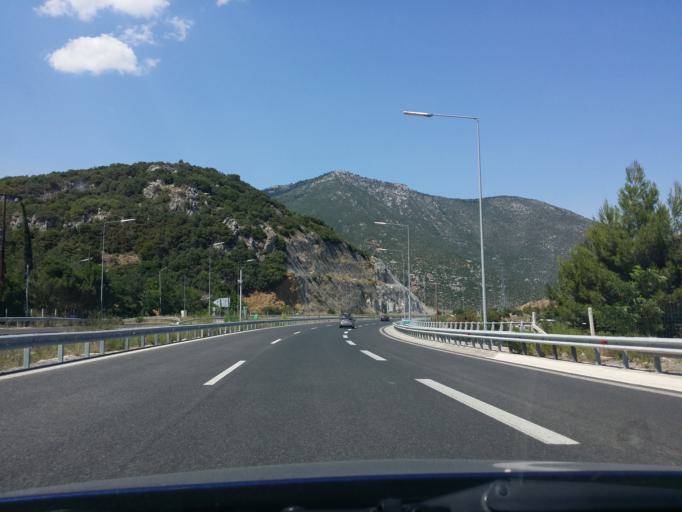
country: GR
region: Peloponnese
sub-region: Nomos Arkadias
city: Tripoli
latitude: 37.6715
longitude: 22.4855
